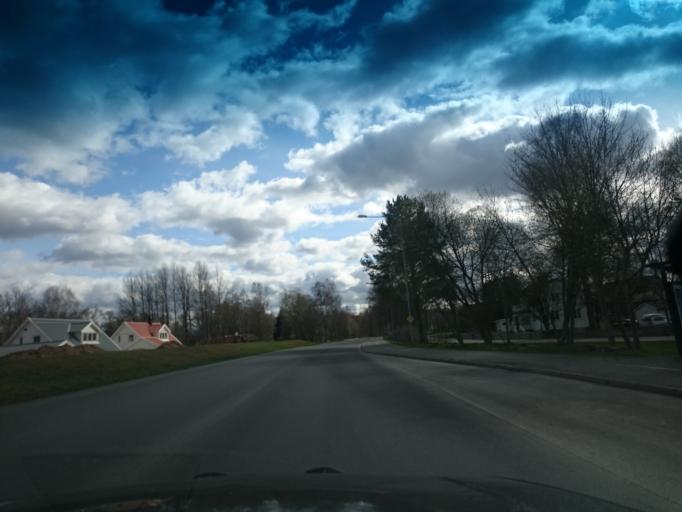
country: SE
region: Joenkoeping
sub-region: Vetlanda Kommun
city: Vetlanda
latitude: 57.4068
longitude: 15.0826
